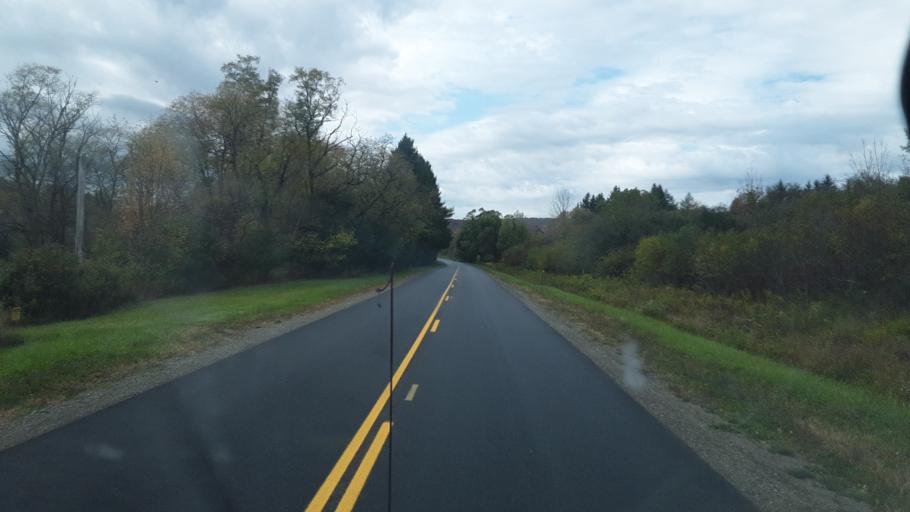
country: US
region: New York
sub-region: Allegany County
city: Alfred
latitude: 42.3696
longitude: -77.7954
